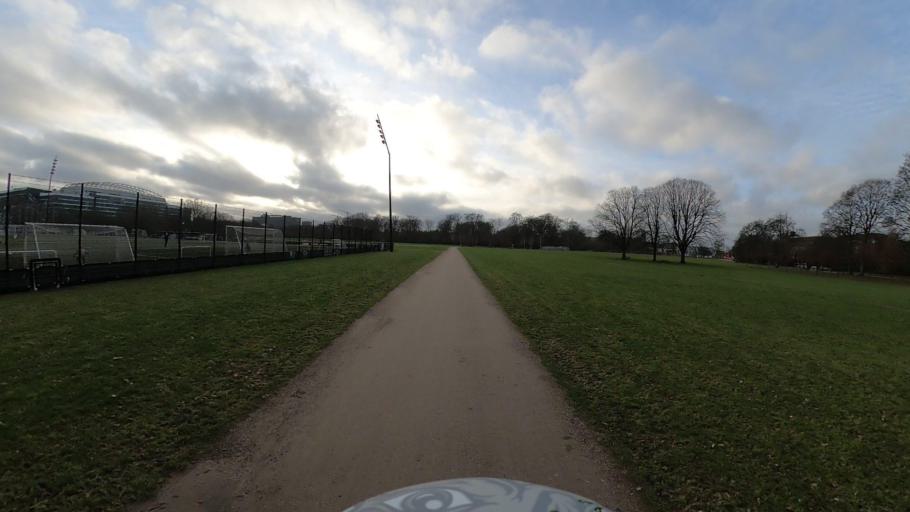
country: DK
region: Capital Region
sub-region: Kobenhavn
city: Copenhagen
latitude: 55.7065
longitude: 12.5696
